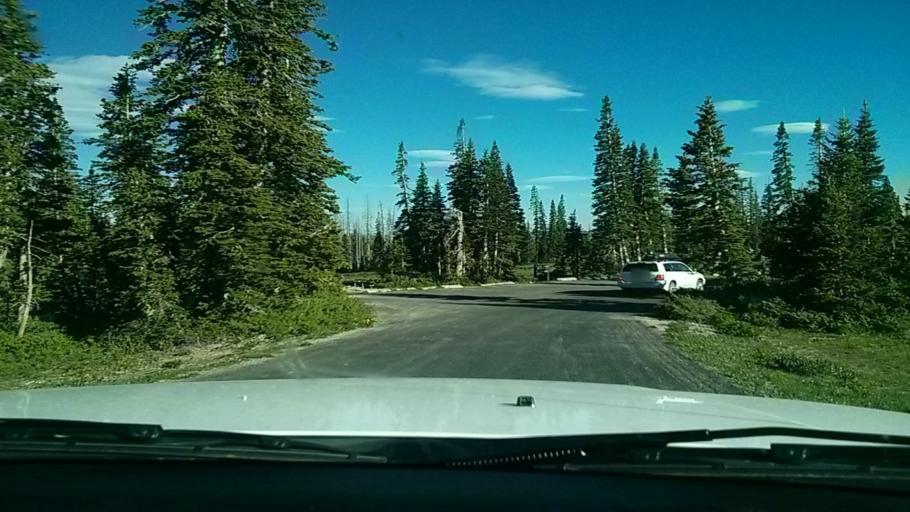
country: US
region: Utah
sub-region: Iron County
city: Parowan
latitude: 37.6129
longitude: -112.8312
